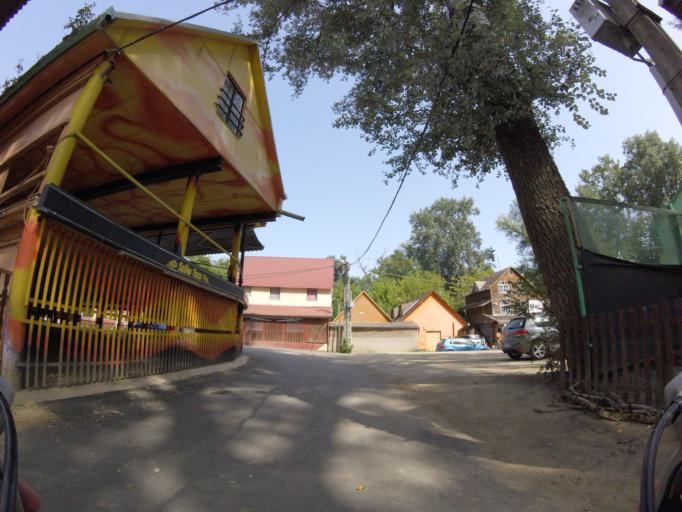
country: HU
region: Szabolcs-Szatmar-Bereg
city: Tarpa
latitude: 48.0616
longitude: 22.5176
